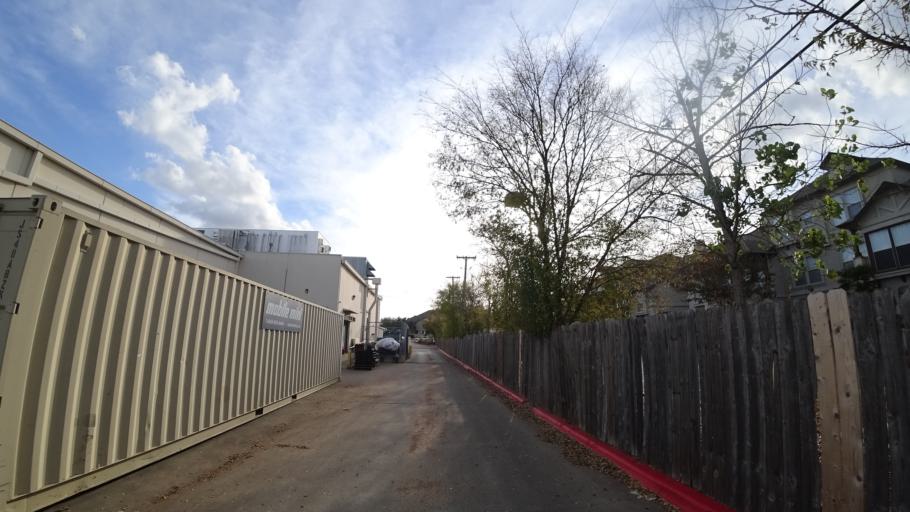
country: US
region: Texas
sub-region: Williamson County
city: Brushy Creek
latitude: 30.5012
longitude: -97.7233
